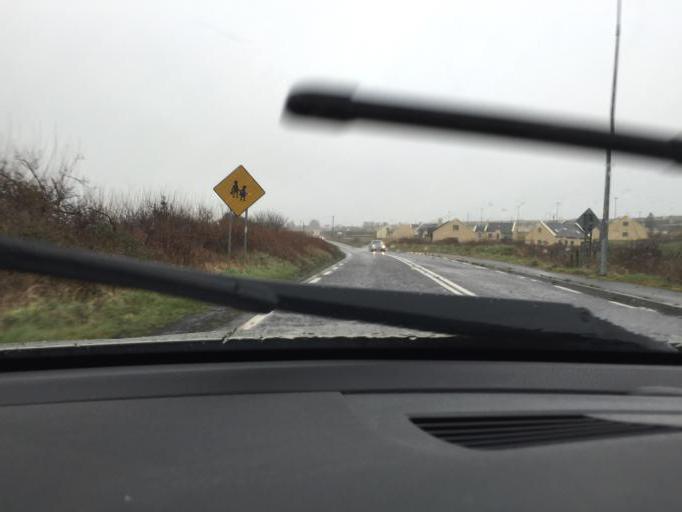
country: IE
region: Munster
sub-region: Ciarrai
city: Dingle
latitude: 52.1439
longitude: -10.1482
